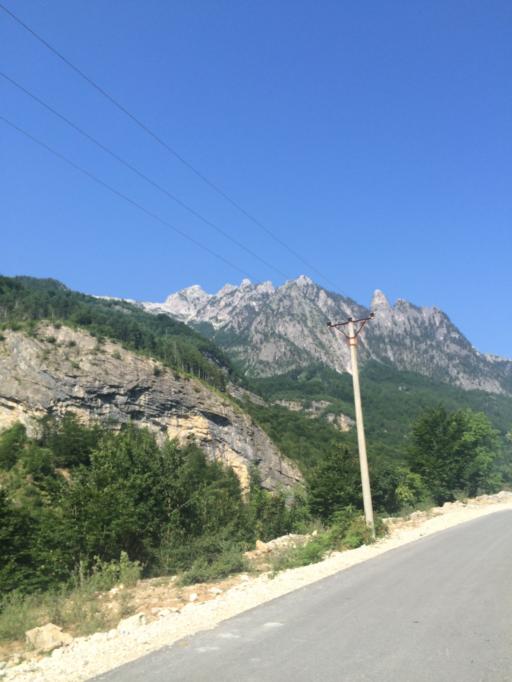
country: AL
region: Kukes
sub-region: Rrethi i Tropojes
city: Valbone
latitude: 42.4401
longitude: 19.9613
